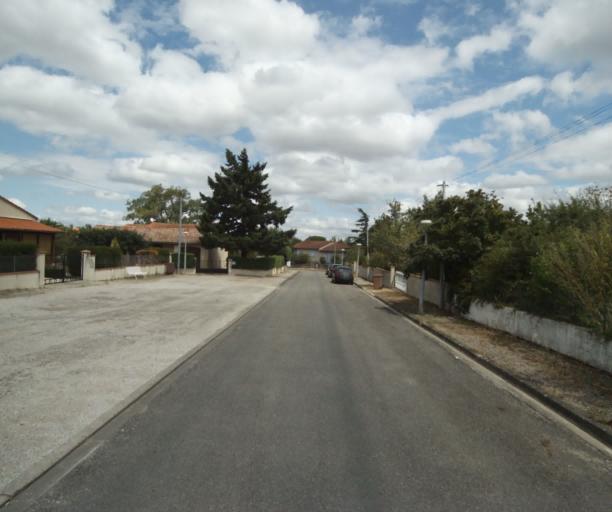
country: FR
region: Midi-Pyrenees
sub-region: Departement de la Haute-Garonne
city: Revel
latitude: 43.4522
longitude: 1.9985
